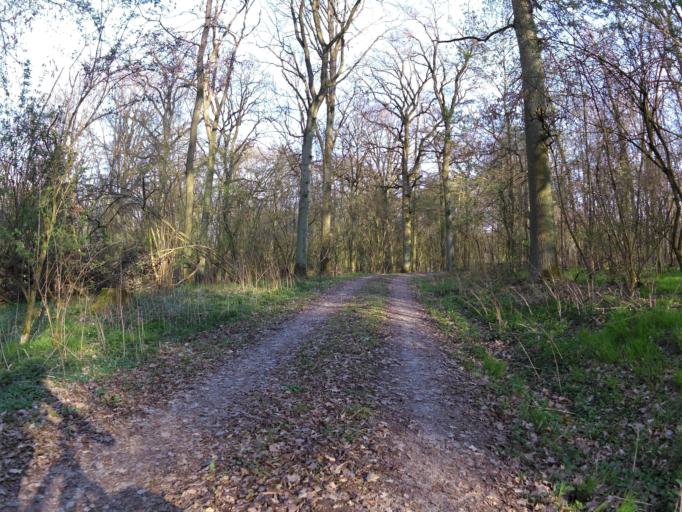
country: DE
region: Bavaria
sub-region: Regierungsbezirk Unterfranken
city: Rottendorf
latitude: 49.7761
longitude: 10.0426
